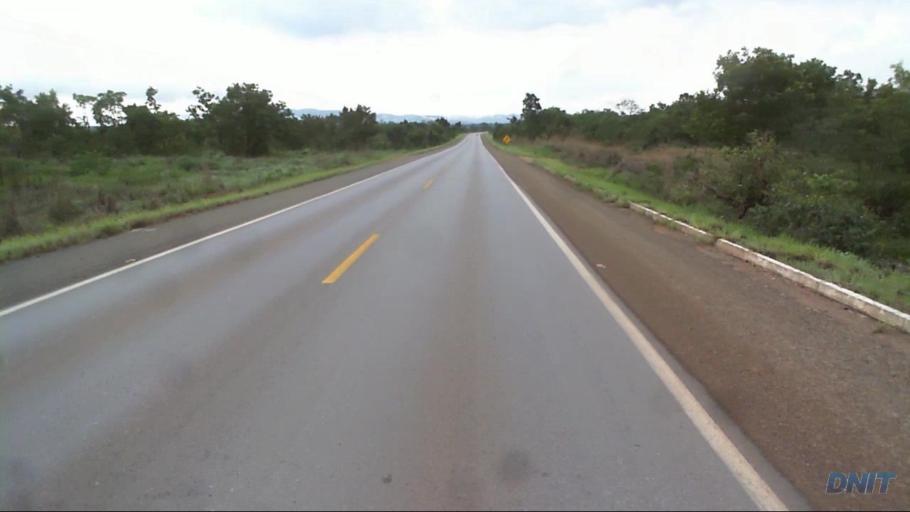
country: BR
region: Goias
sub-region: Uruacu
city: Uruacu
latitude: -14.7343
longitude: -49.0881
